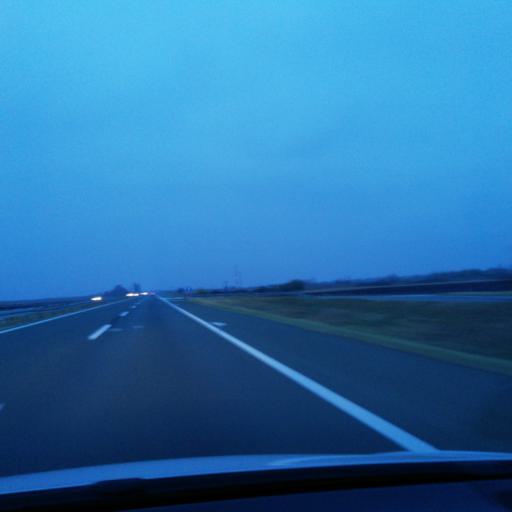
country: RS
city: Sasinci
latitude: 44.9787
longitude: 19.7340
